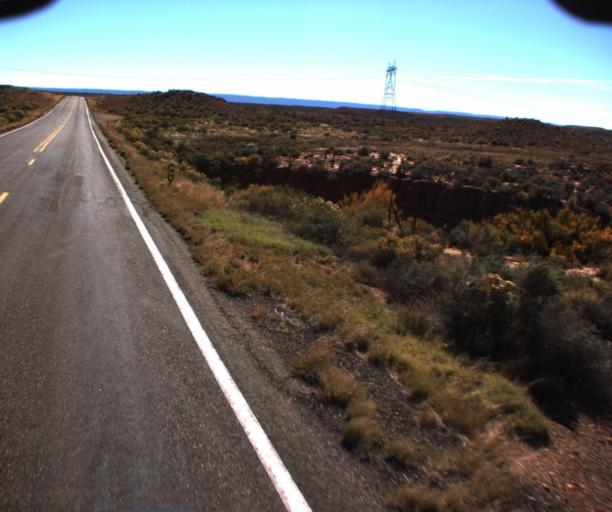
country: US
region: Arizona
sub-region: Coconino County
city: Fredonia
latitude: 36.9179
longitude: -112.4320
